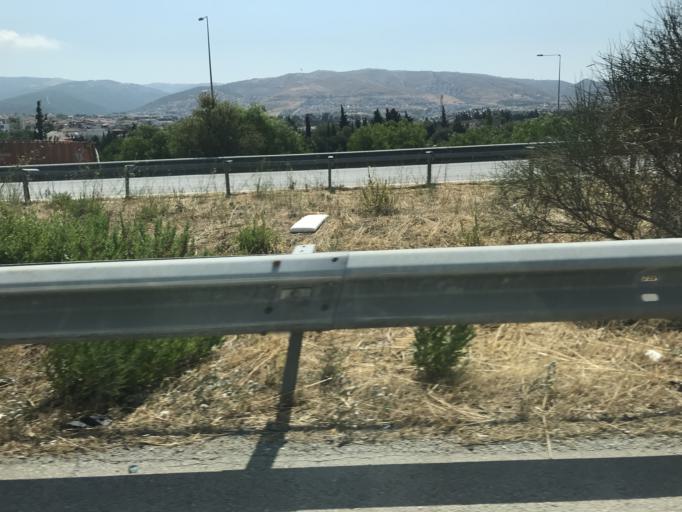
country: TR
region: Izmir
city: Urla
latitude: 38.3684
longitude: 26.8699
